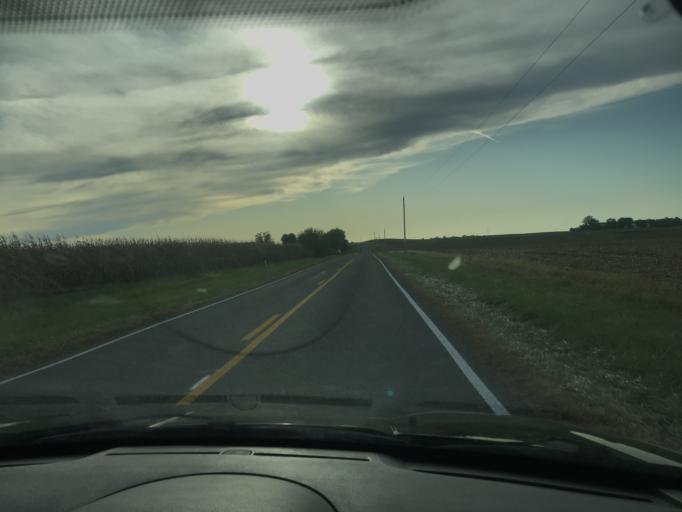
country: US
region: Ohio
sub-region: Logan County
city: West Liberty
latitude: 40.2122
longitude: -83.6955
